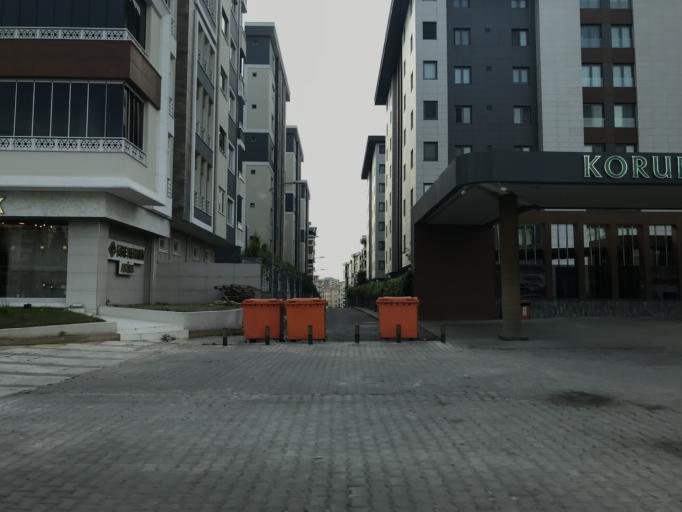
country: TR
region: Gaziantep
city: Sehitkamil
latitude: 37.0753
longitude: 37.3421
